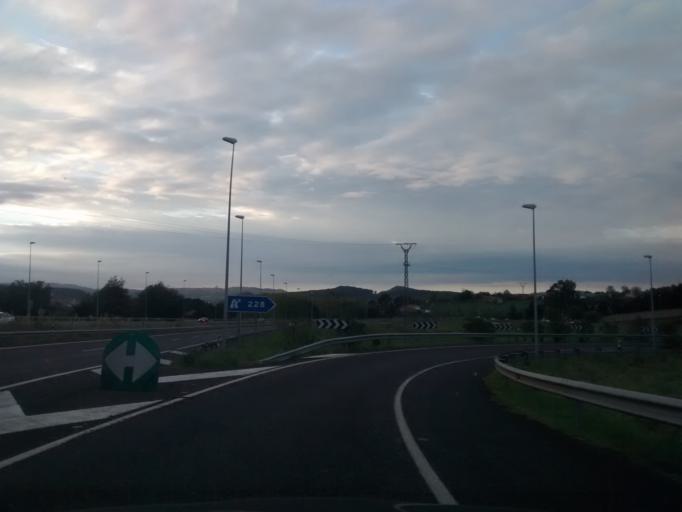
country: ES
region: Cantabria
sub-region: Provincia de Cantabria
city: Torrelavega
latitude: 43.3478
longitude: -4.0306
